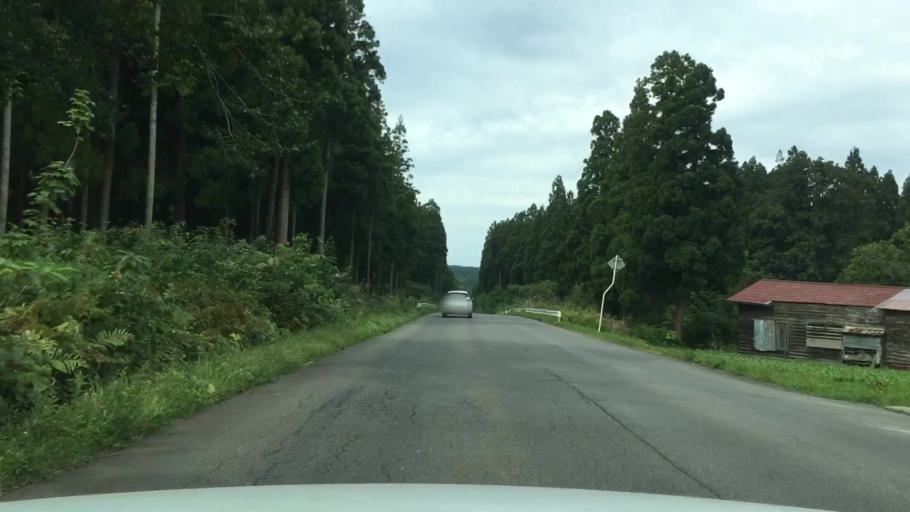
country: JP
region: Aomori
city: Shimokizukuri
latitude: 40.7105
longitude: 140.2727
